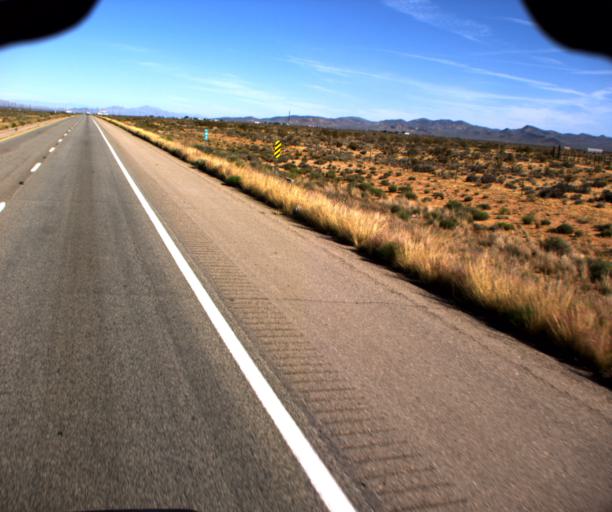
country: US
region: Arizona
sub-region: Mohave County
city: Dolan Springs
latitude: 35.5195
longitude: -114.3452
